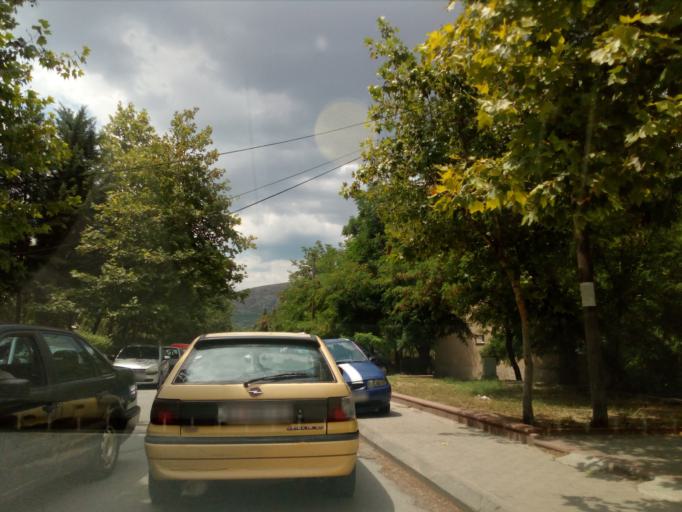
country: MK
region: Veles
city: Veles
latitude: 41.7150
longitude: 21.7653
